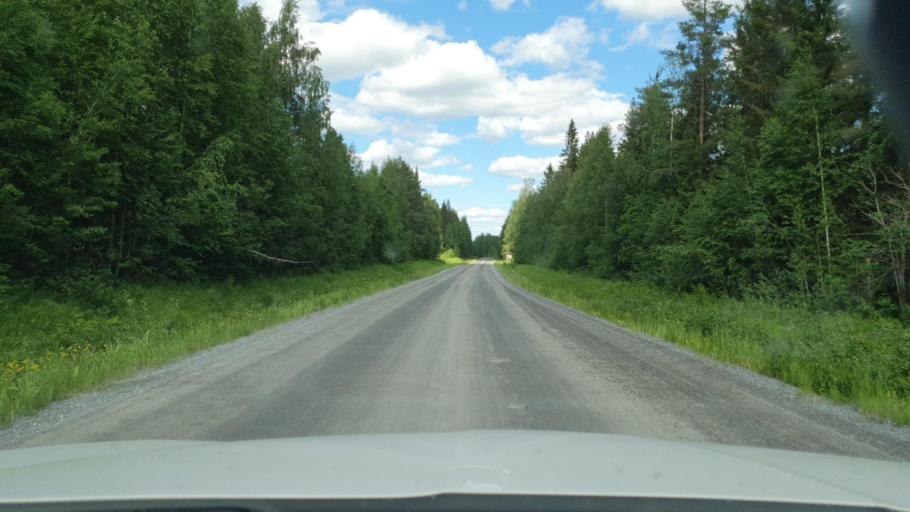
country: SE
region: Vaesterbotten
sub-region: Skelleftea Kommun
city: Forsbacka
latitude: 64.8270
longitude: 20.4979
